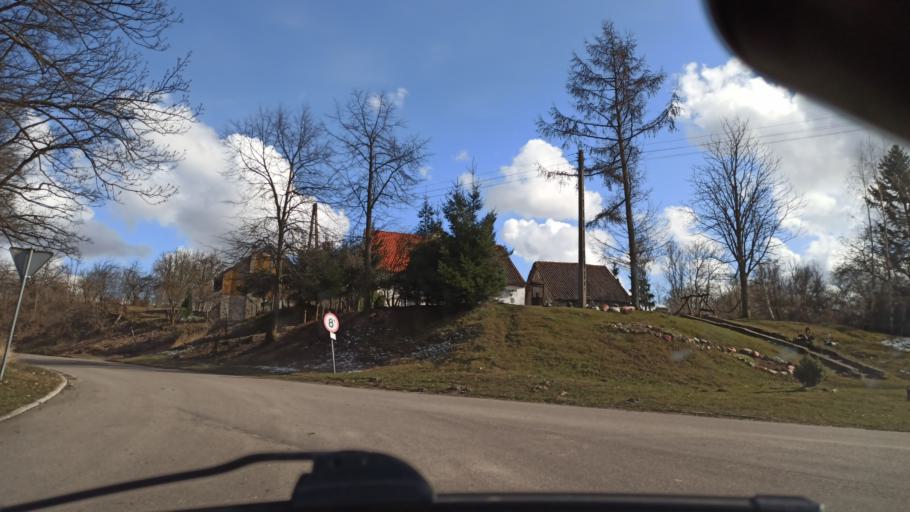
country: PL
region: Warmian-Masurian Voivodeship
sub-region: Powiat elblaski
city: Tolkmicko
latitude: 54.2657
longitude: 19.4781
